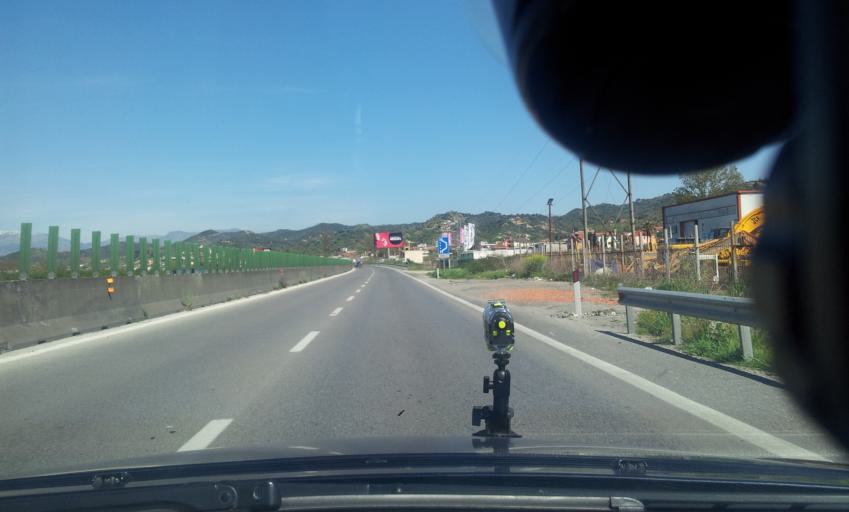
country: AL
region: Durres
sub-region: Rrethi i Durresit
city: Maminas
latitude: 41.3722
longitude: 19.6095
